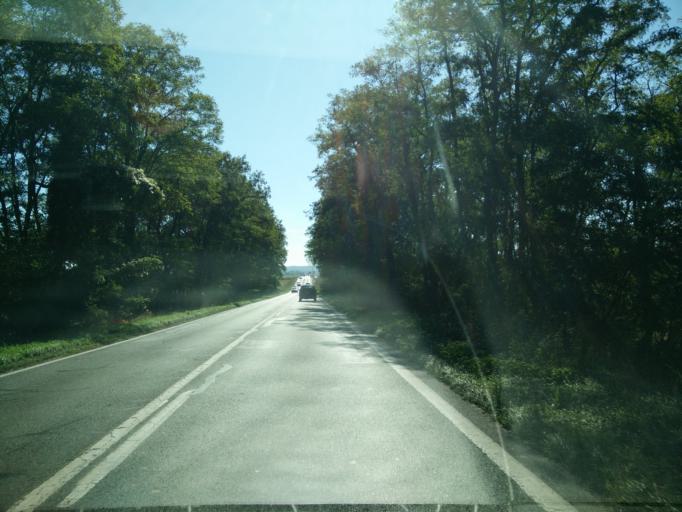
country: FR
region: Ile-de-France
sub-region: Departement de Seine-et-Marne
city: Mitry-Mory
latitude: 48.9861
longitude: 2.6581
